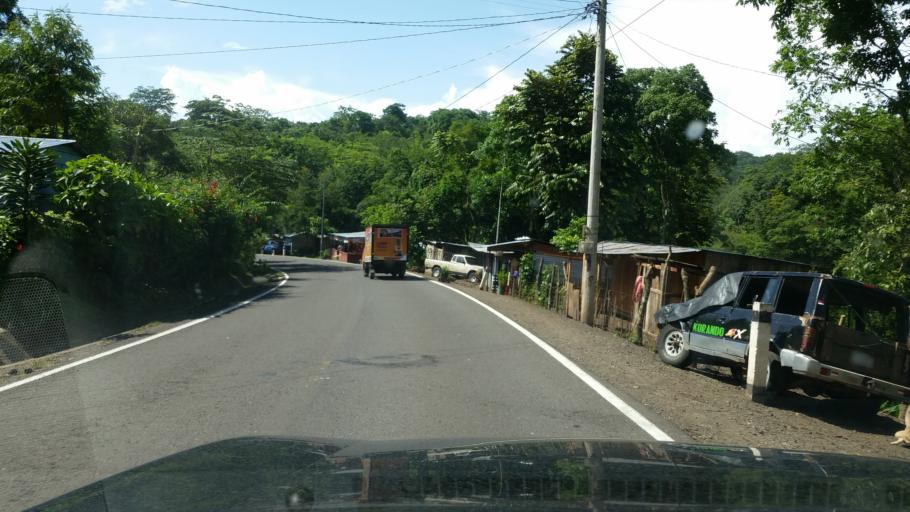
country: NI
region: Matagalpa
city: San Ramon
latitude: 12.9999
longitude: -85.8102
